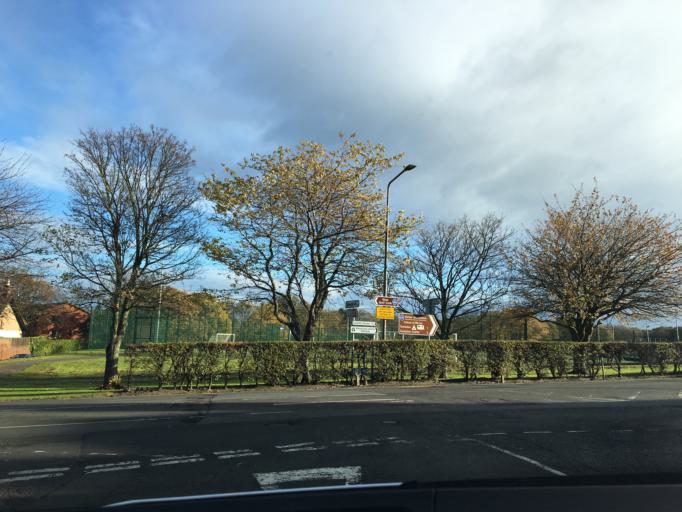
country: GB
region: Scotland
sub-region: East Lothian
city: North Berwick
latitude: 56.0553
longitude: -2.7101
